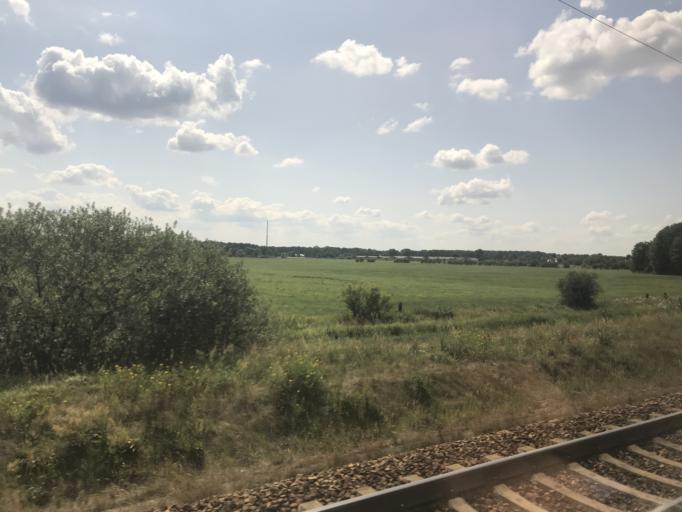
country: DE
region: Brandenburg
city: Briesen
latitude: 52.3442
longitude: 14.2927
